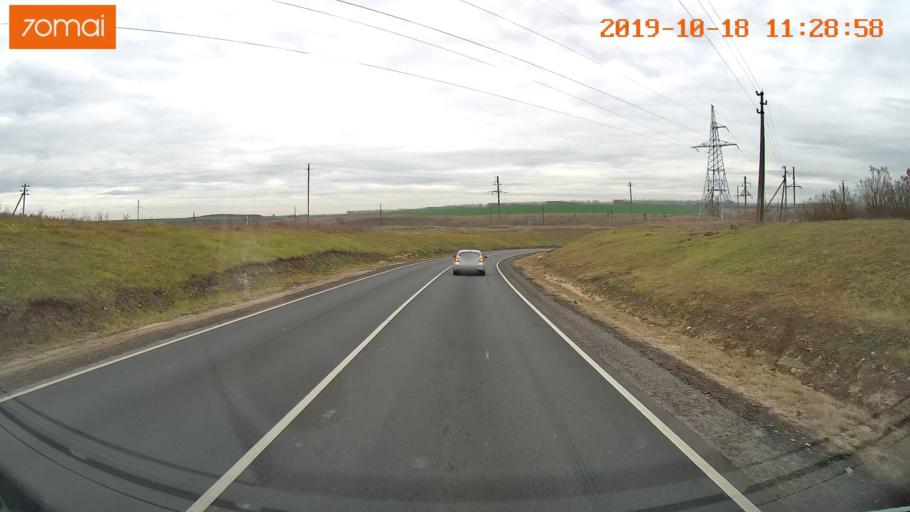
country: RU
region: Tula
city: Kimovsk
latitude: 54.1574
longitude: 38.6698
